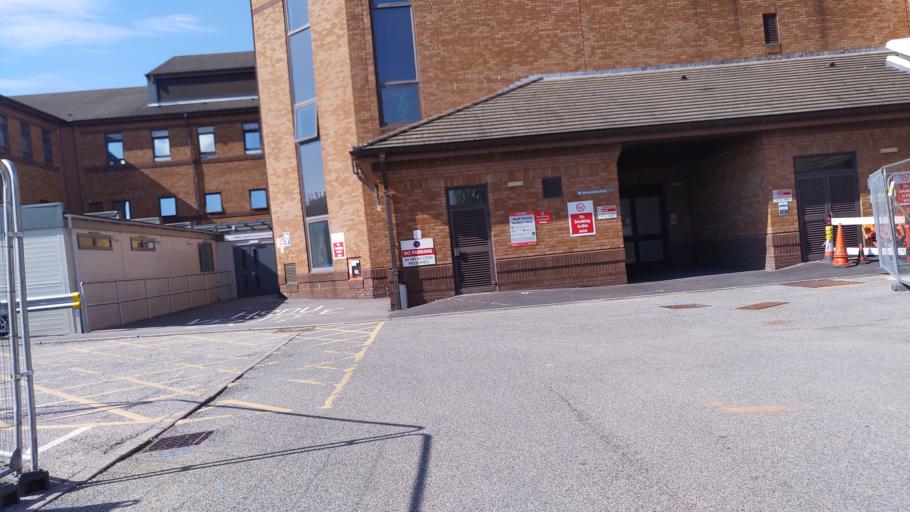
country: GB
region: England
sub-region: Lancashire
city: Chorley
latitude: 53.6653
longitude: -2.6366
